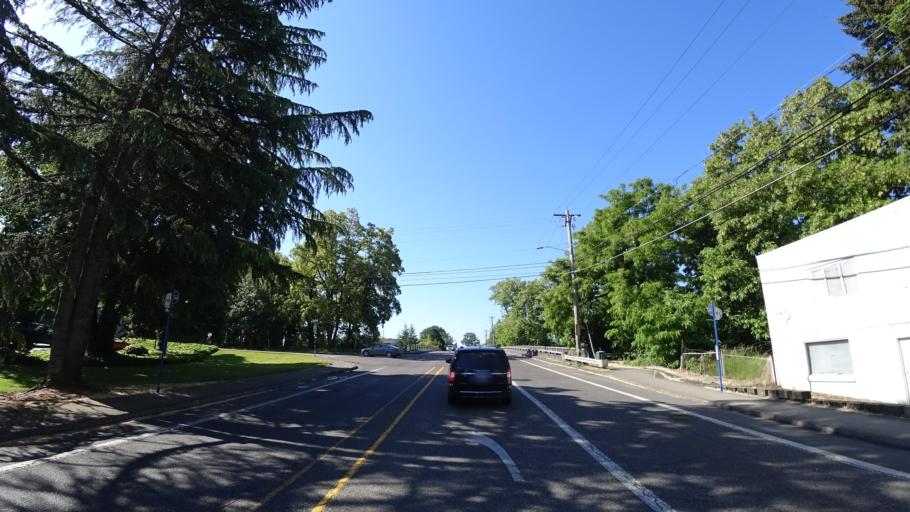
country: US
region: Oregon
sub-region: Washington County
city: Tigard
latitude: 45.4384
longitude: -122.7654
